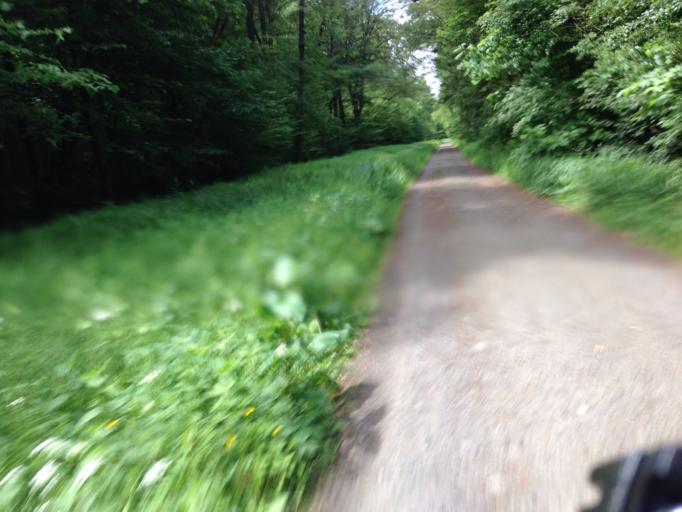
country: DE
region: Hesse
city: Bruchkobel
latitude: 50.1670
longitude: 8.9266
